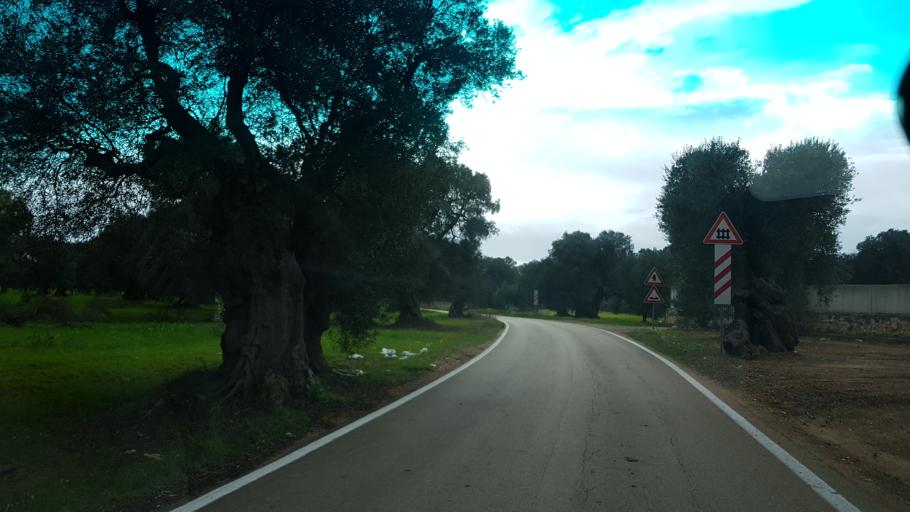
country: IT
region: Apulia
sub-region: Provincia di Brindisi
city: San Vito dei Normanni
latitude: 40.7021
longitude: 17.7639
